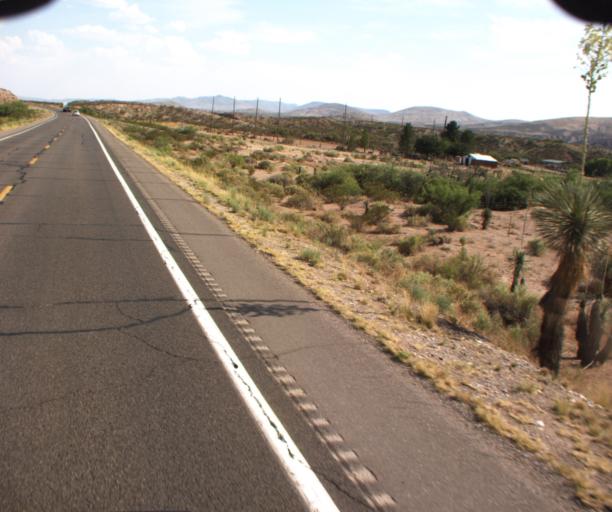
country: US
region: Arizona
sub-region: Greenlee County
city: Clifton
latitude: 32.7875
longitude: -109.1593
